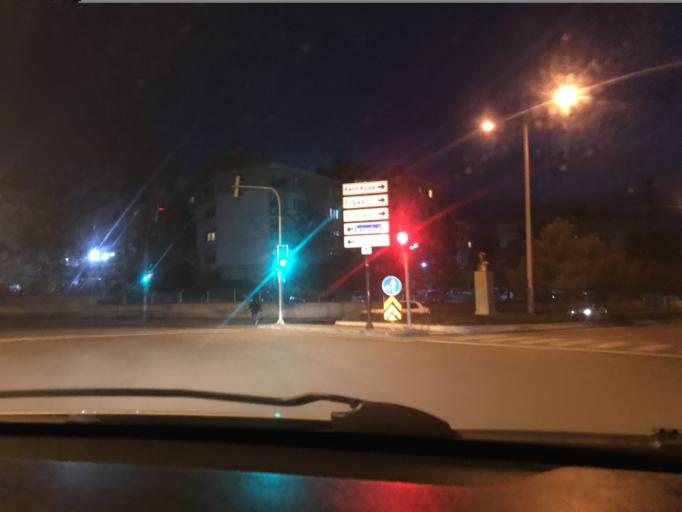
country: TR
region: Ankara
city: Batikent
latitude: 39.9583
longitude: 32.7290
